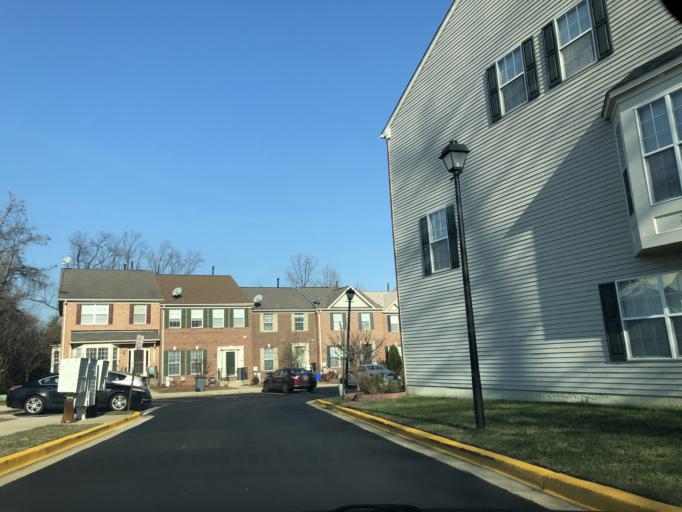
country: US
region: Maryland
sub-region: Montgomery County
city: Burtonsville
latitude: 39.1030
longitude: -76.9321
